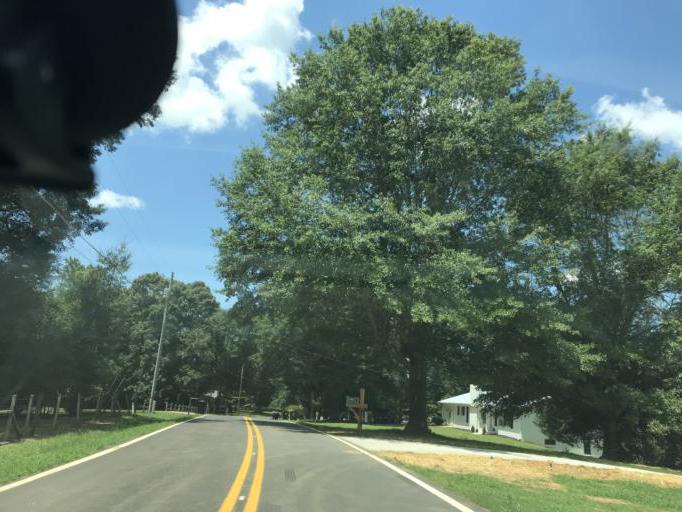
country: US
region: Georgia
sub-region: Forsyth County
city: Cumming
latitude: 34.2674
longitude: -84.2398
